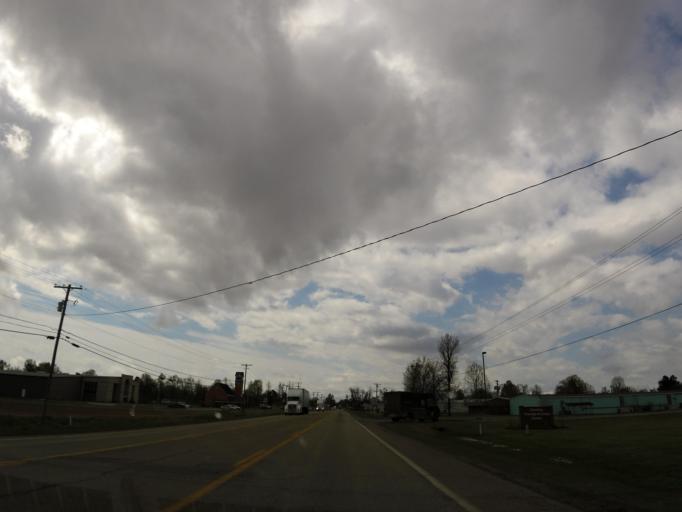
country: US
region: Arkansas
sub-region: Clay County
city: Corning
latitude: 36.4205
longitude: -90.5863
